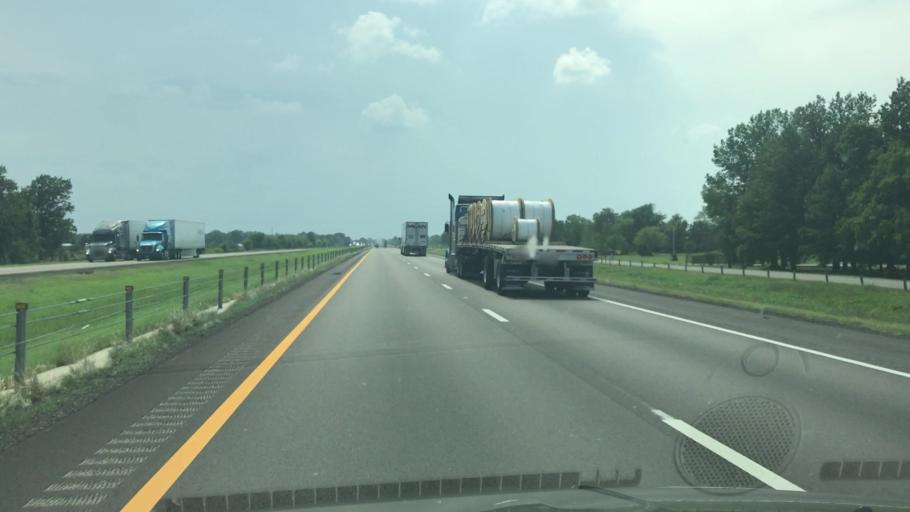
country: US
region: Arkansas
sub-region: Crittenden County
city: Earle
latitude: 35.1433
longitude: -90.4188
